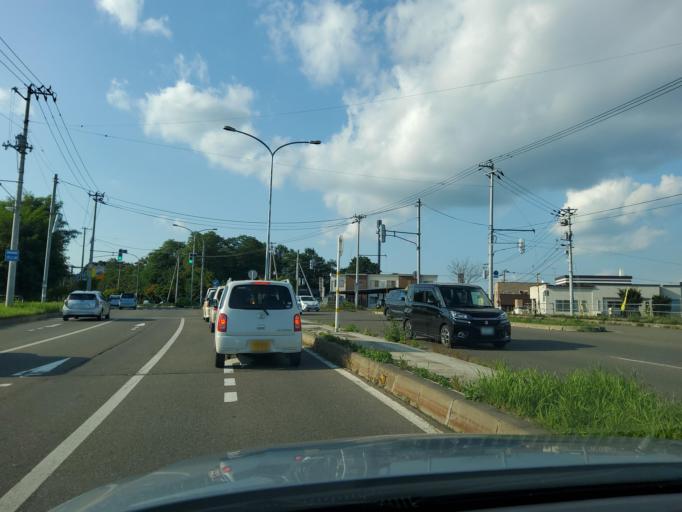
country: JP
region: Hokkaido
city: Obihiro
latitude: 42.9002
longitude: 143.1740
